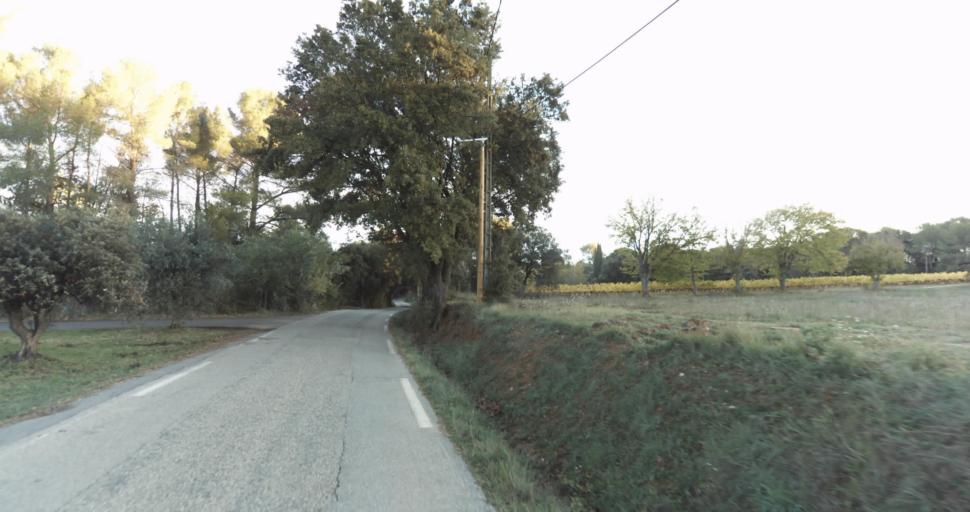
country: FR
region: Provence-Alpes-Cote d'Azur
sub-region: Departement des Bouches-du-Rhone
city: Venelles
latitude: 43.5742
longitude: 5.4836
